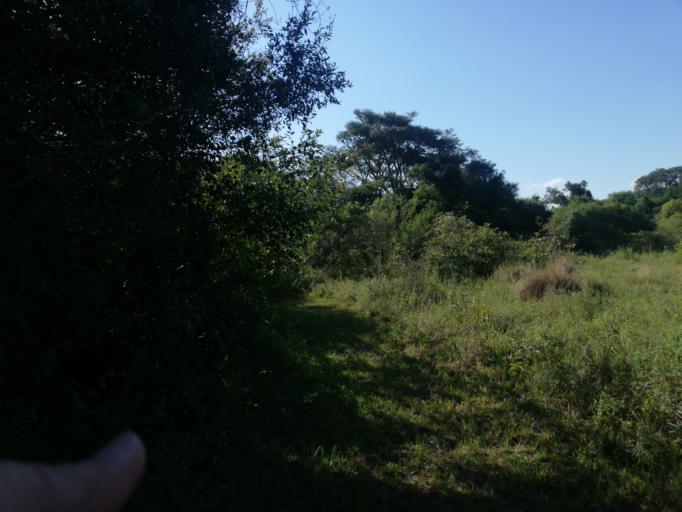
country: AR
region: Corrientes
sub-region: Departamento de San Miguel
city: San Miguel
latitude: -27.9876
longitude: -57.5421
